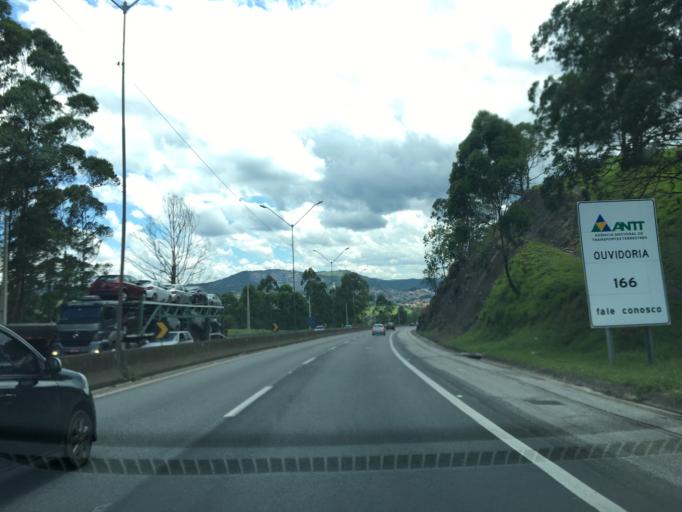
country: BR
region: Sao Paulo
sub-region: Mairipora
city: Mairipora
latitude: -23.3024
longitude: -46.5725
